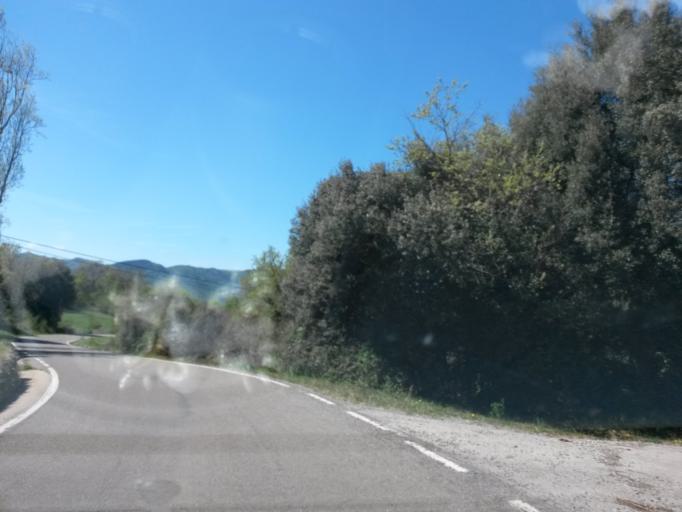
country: ES
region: Catalonia
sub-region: Provincia de Girona
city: Sant Cristofol de les Fonts
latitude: 42.1732
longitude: 2.5220
